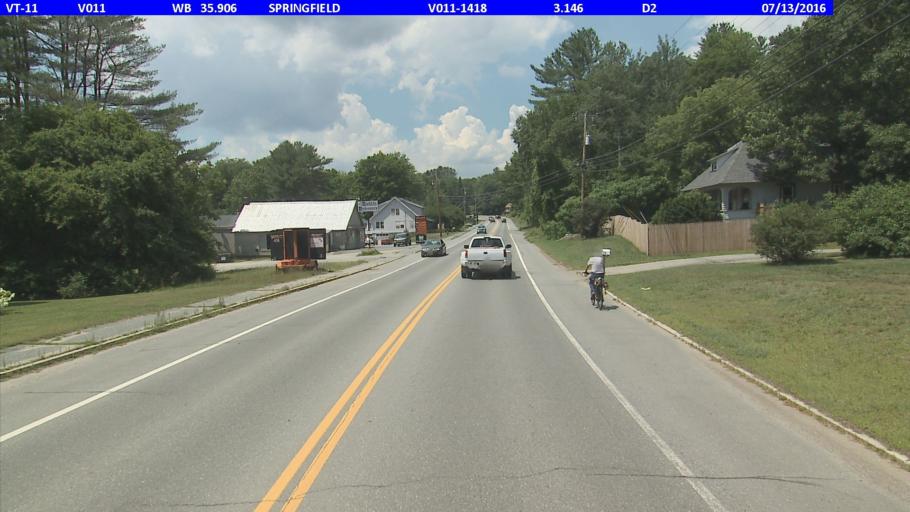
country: US
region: Vermont
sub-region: Windsor County
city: Springfield
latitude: 43.2990
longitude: -72.5021
